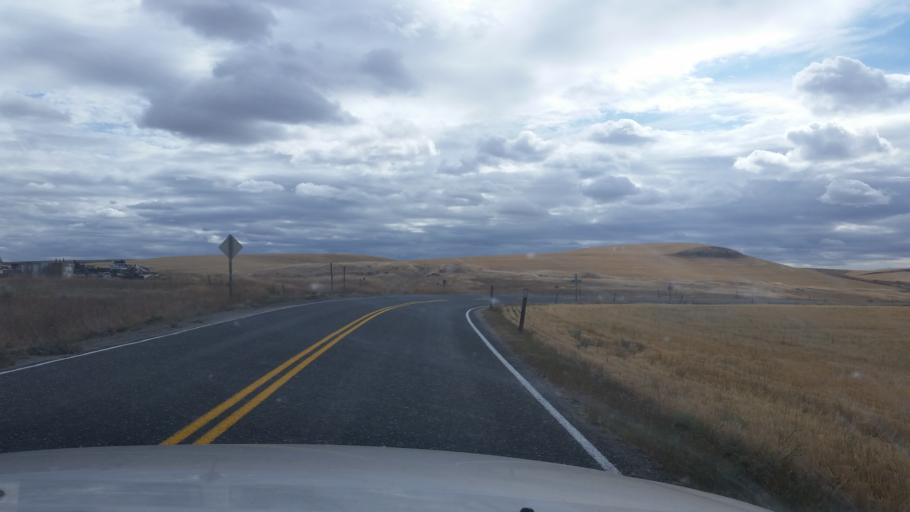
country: US
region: Washington
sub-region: Lincoln County
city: Davenport
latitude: 47.5022
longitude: -117.9543
